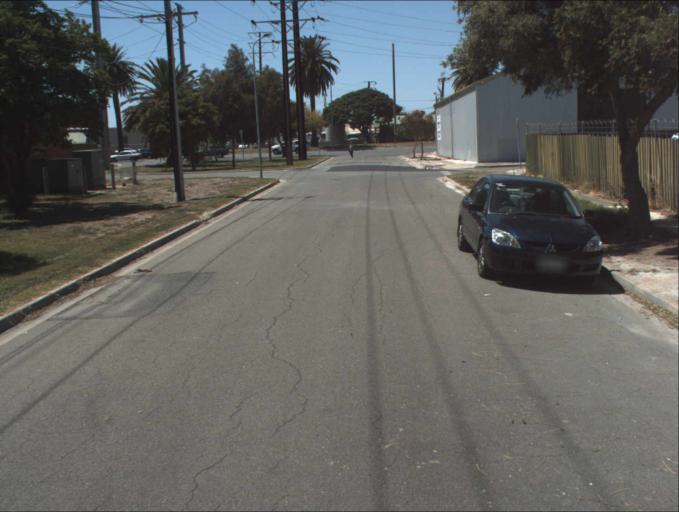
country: AU
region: South Australia
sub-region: Port Adelaide Enfield
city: Alberton
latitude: -34.8534
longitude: 138.5081
